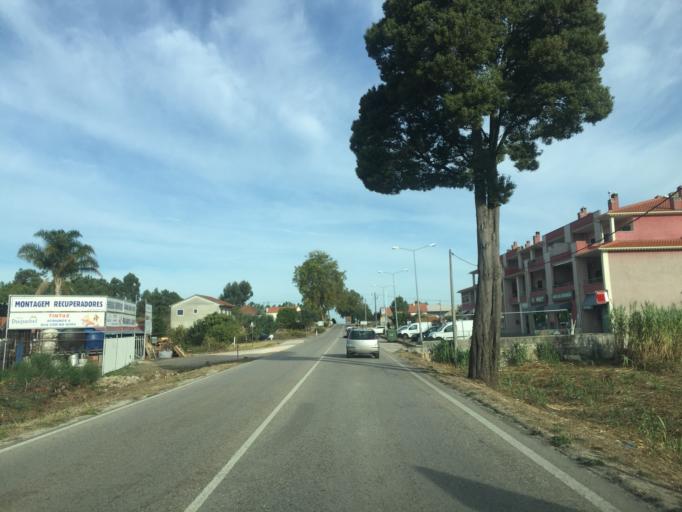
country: PT
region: Leiria
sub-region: Pombal
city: Lourical
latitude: 39.9601
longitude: -8.7878
